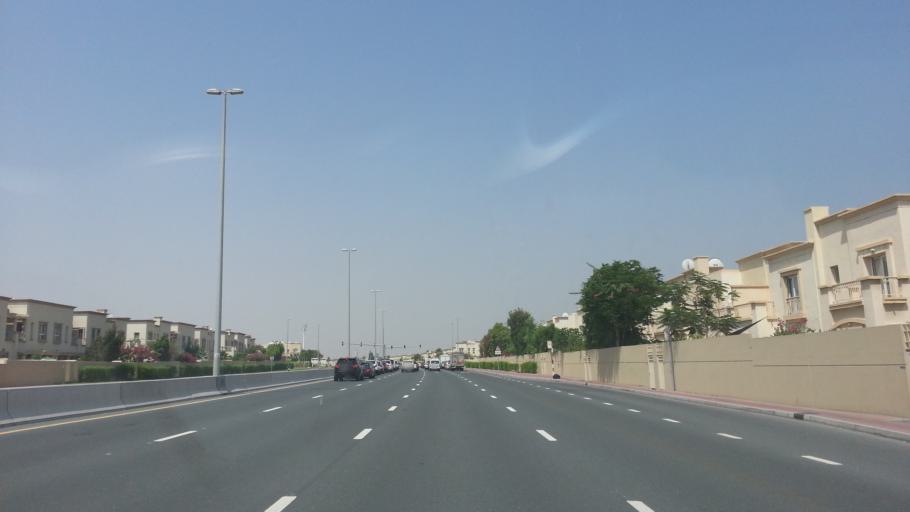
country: AE
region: Dubai
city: Dubai
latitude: 25.0597
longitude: 55.1807
